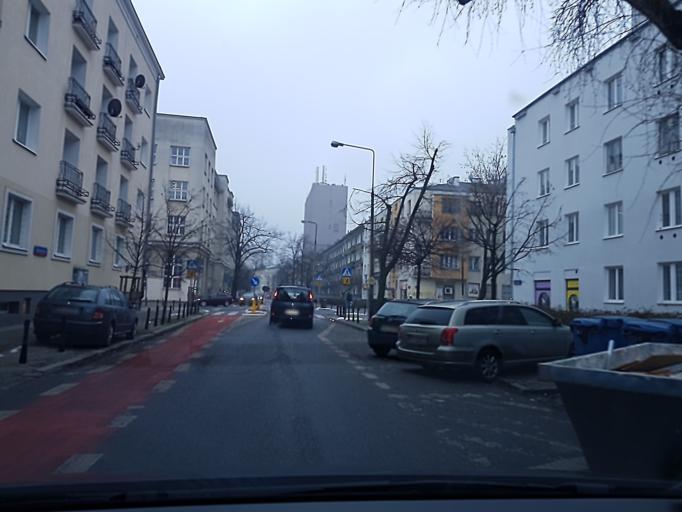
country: PL
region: Masovian Voivodeship
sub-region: Warszawa
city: Srodmiescie
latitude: 52.2065
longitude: 21.0135
